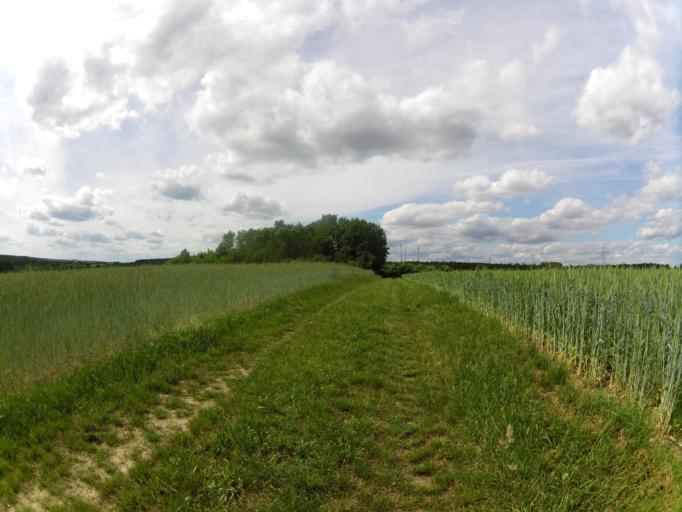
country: DE
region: Bavaria
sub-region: Regierungsbezirk Unterfranken
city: Ochsenfurt
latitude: 49.6956
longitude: 10.0654
